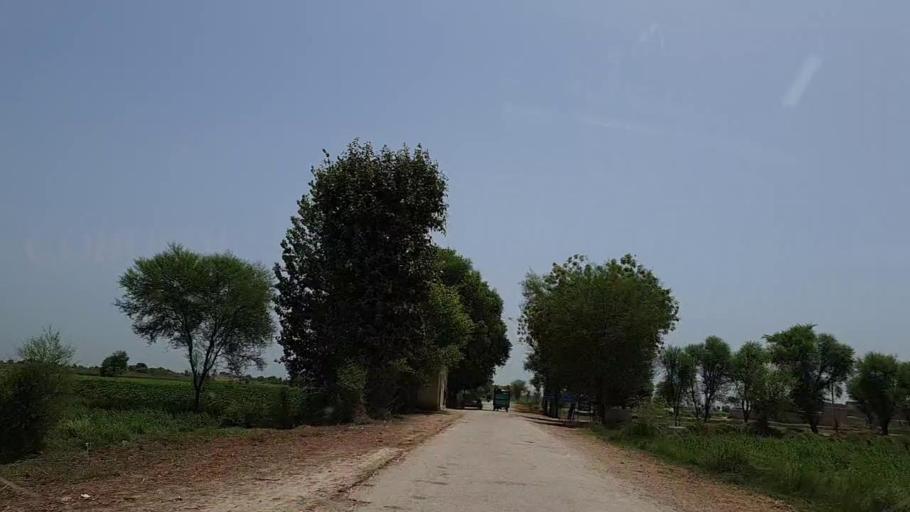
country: PK
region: Sindh
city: Tharu Shah
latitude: 26.9647
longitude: 68.0513
